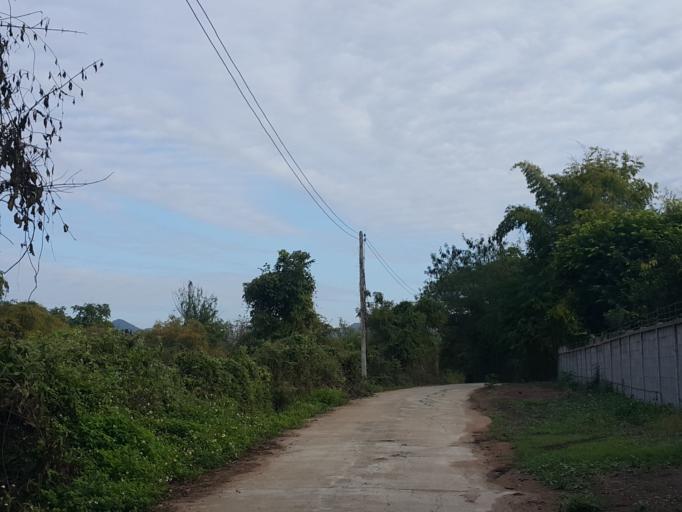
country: TH
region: Lampang
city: Mae Mo
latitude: 18.2511
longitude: 99.6015
